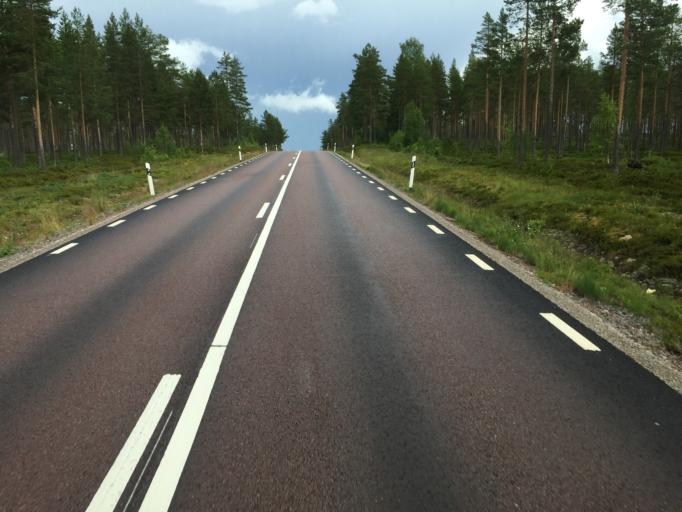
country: SE
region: Dalarna
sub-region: Malung-Saelens kommun
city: Malung
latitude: 60.8244
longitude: 14.0161
